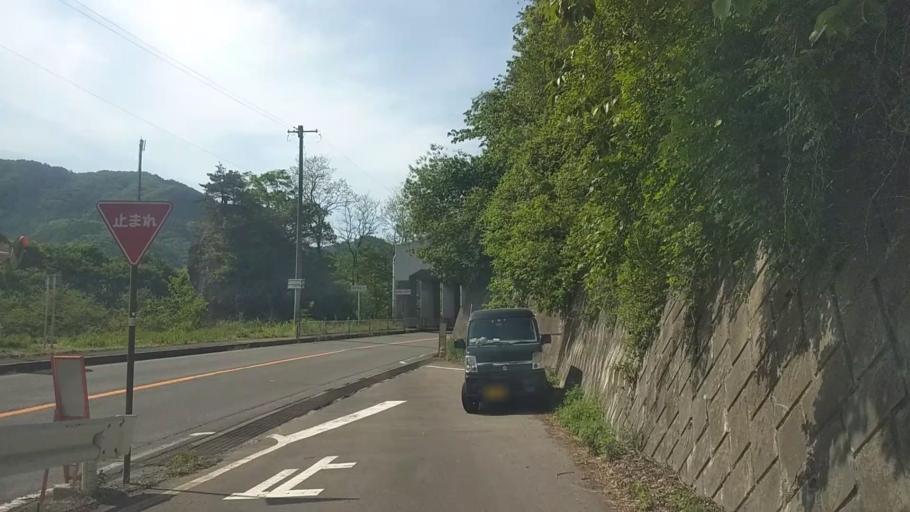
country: JP
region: Nagano
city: Saku
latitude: 36.1036
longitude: 138.4814
